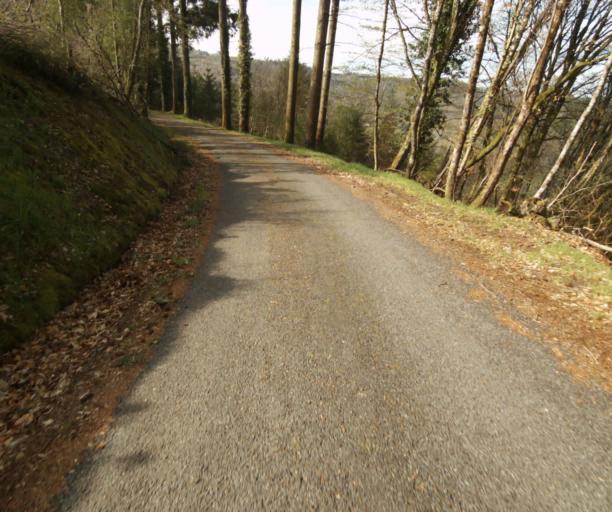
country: FR
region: Limousin
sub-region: Departement de la Correze
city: Naves
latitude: 45.3258
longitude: 1.8168
